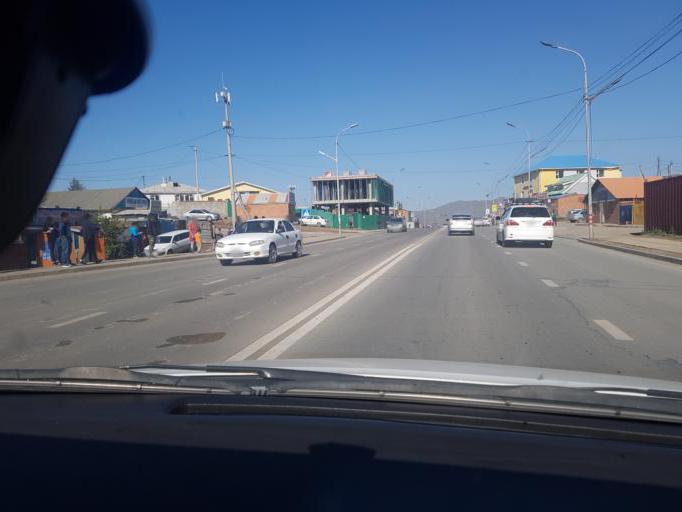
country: MN
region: Ulaanbaatar
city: Ulaanbaatar
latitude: 47.9534
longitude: 106.8532
